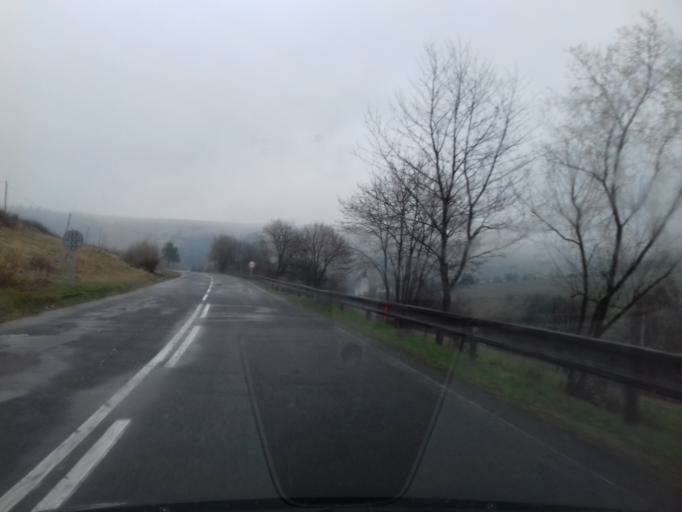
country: SK
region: Presovsky
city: Stara L'ubovna
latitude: 49.3567
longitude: 20.6903
